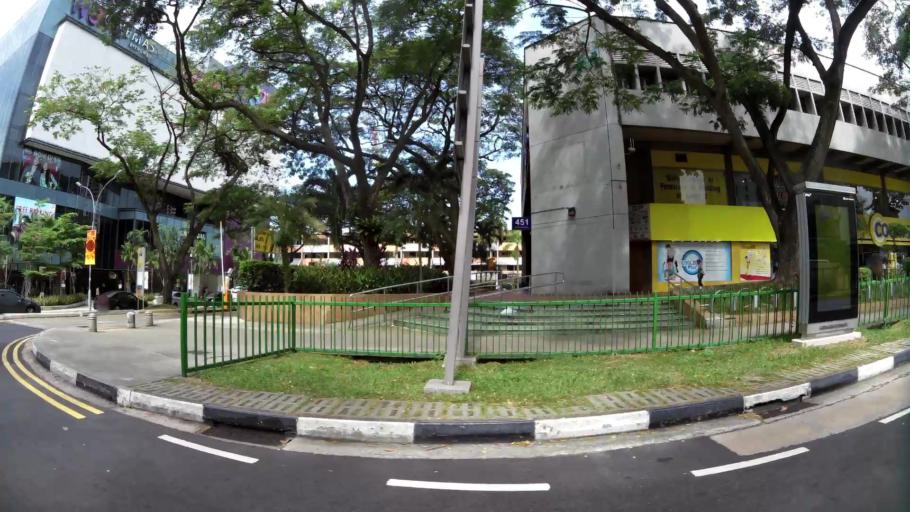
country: SG
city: Singapore
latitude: 1.3121
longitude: 103.7656
